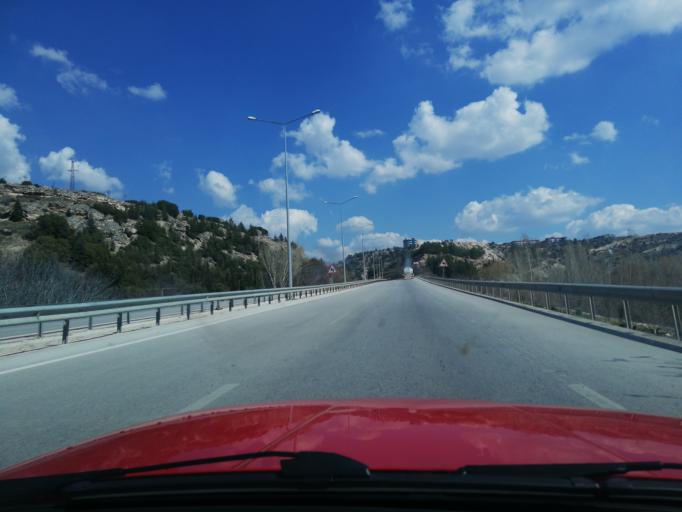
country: TR
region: Burdur
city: Burdur
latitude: 37.6984
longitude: 30.3265
